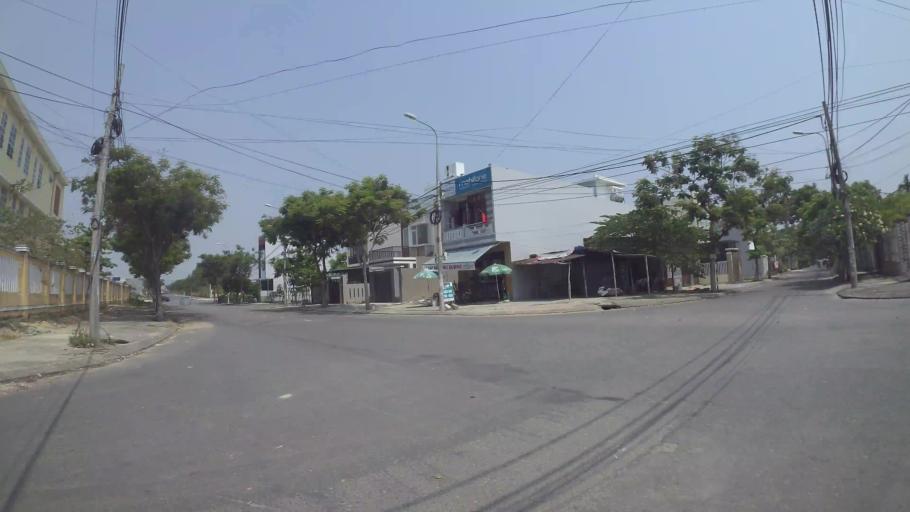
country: VN
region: Da Nang
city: Ngu Hanh Son
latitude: 16.0138
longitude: 108.2524
